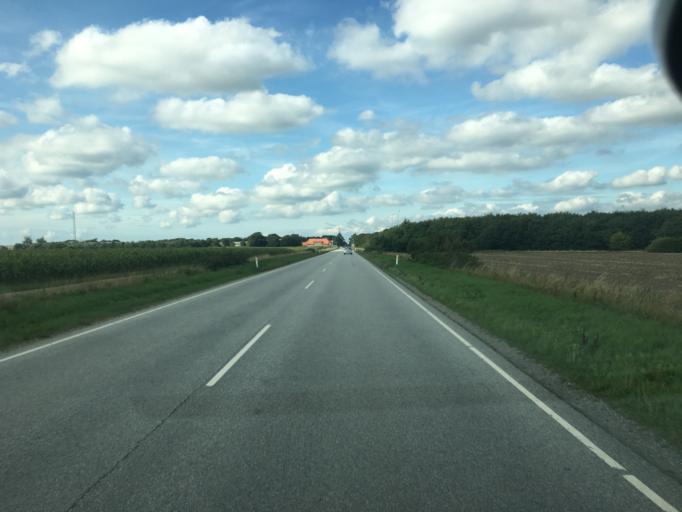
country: DK
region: South Denmark
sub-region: Tonder Kommune
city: Tonder
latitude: 54.9730
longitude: 8.8652
